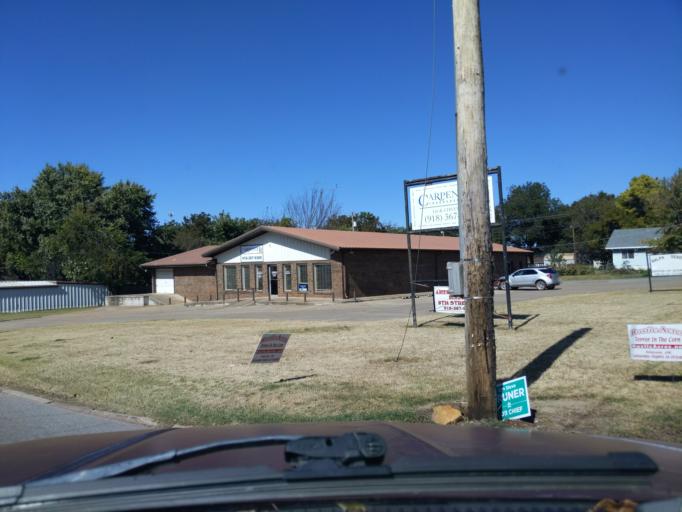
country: US
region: Oklahoma
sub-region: Creek County
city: Bristow
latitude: 35.8284
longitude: -96.3873
